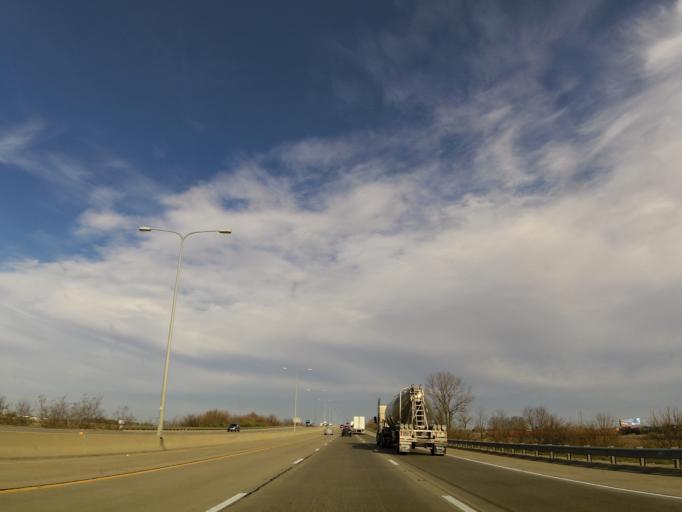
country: US
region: Illinois
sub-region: McLean County
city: Bloomington
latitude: 40.4985
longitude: -89.0285
